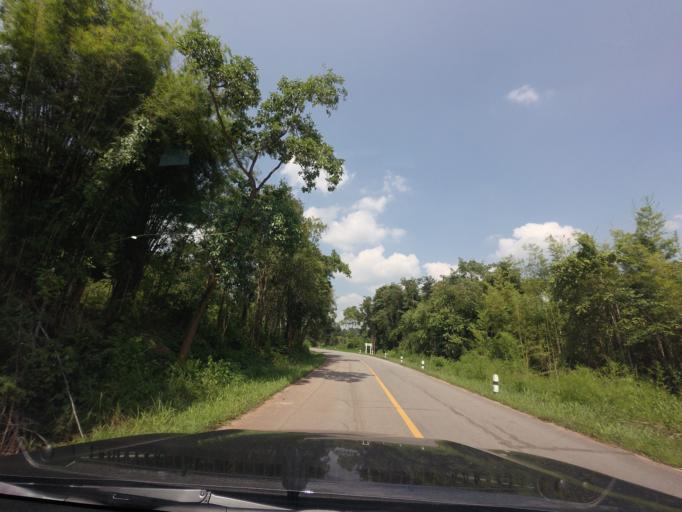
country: TH
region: Uttaradit
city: Fak Tha
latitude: 17.9022
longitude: 100.9805
